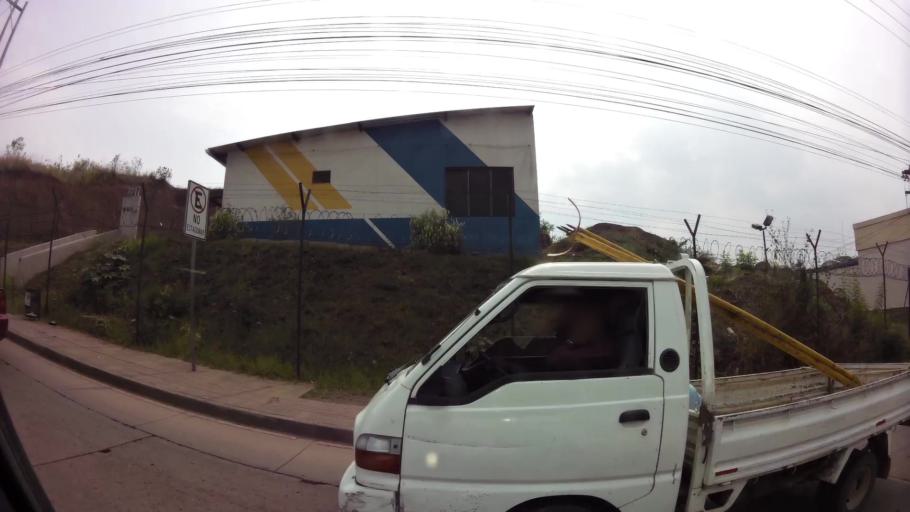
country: HN
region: Francisco Morazan
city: Tegucigalpa
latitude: 14.0707
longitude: -87.1845
